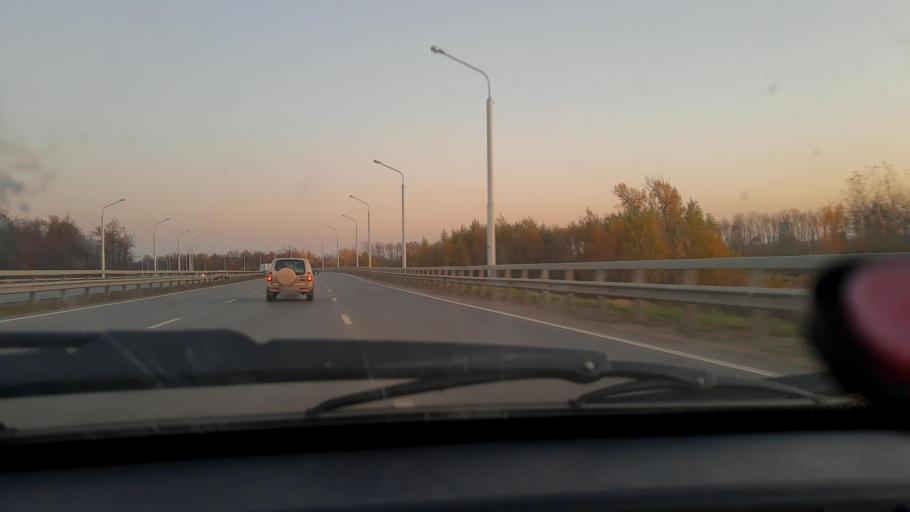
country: RU
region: Bashkortostan
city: Mikhaylovka
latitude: 54.7866
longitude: 55.9085
